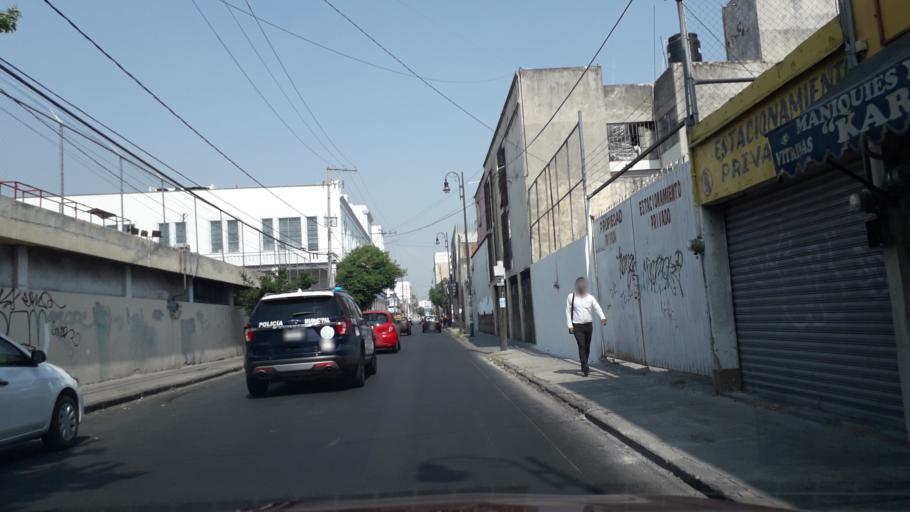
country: MX
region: Puebla
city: Puebla
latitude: 19.0439
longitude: -98.2071
